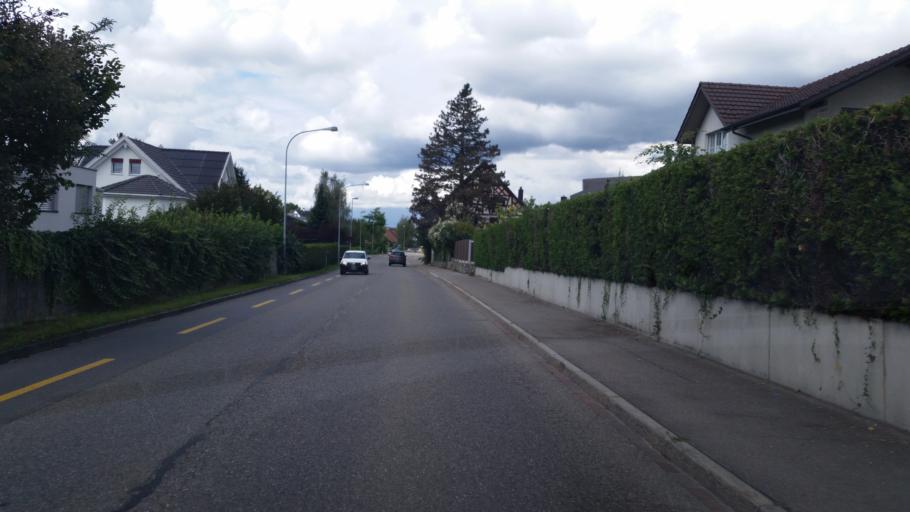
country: CH
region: Zurich
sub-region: Bezirk Affoltern
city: Ottenbach
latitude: 47.2764
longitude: 8.4093
